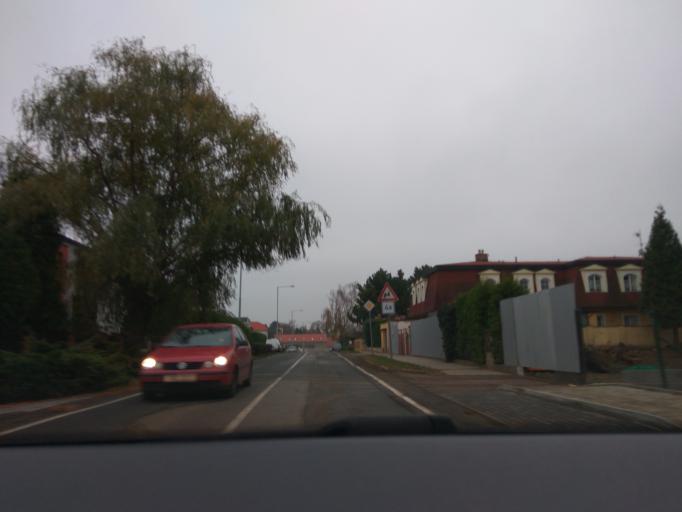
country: CZ
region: Central Bohemia
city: Hovorcovice
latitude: 50.1653
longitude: 14.5238
